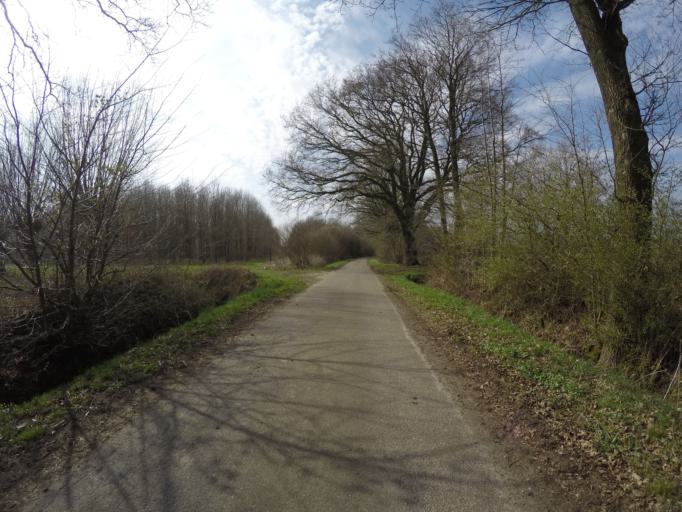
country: DE
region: Schleswig-Holstein
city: Borstel-Hohenraden
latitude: 53.7187
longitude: 9.8393
